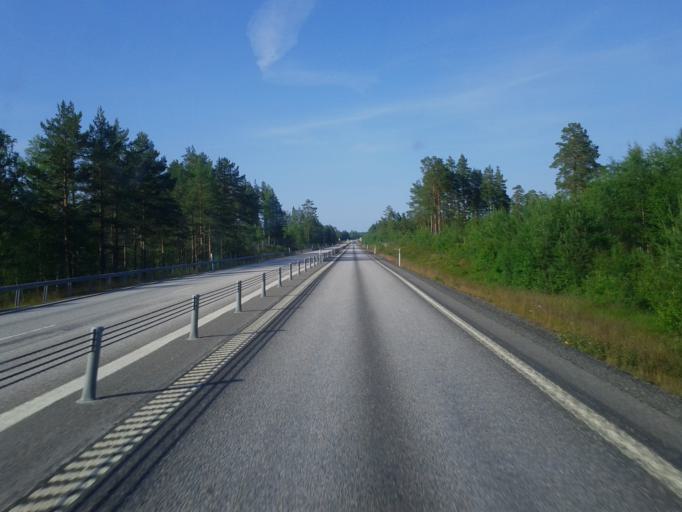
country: SE
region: Vaesterbotten
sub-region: Umea Kommun
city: Saevar
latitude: 63.9430
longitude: 20.6542
